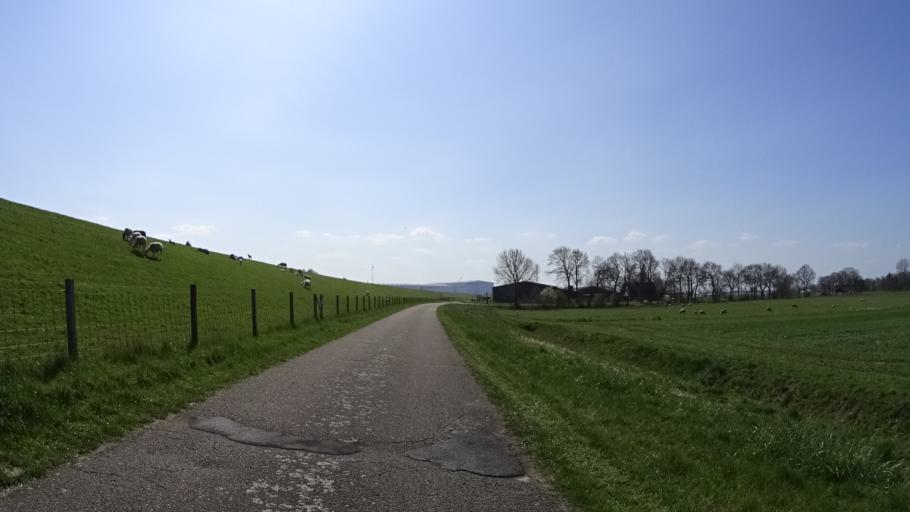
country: DE
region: Lower Saxony
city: Papenburg
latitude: 53.1159
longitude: 7.3708
